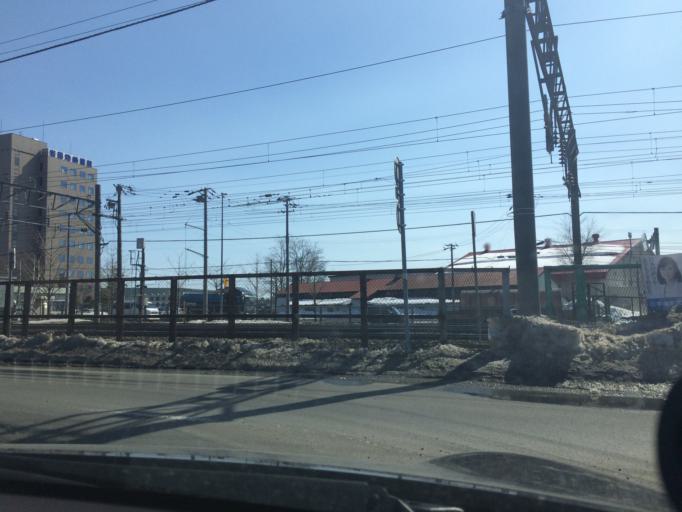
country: JP
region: Hokkaido
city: Sapporo
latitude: 43.0694
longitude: 141.3812
